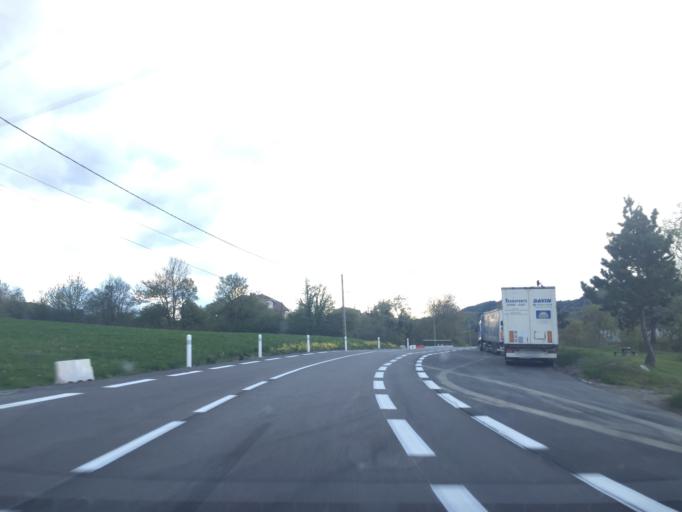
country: FR
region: Rhone-Alpes
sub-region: Departement de l'Isere
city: La Motte-Saint-Martin
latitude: 44.8897
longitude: 5.6156
